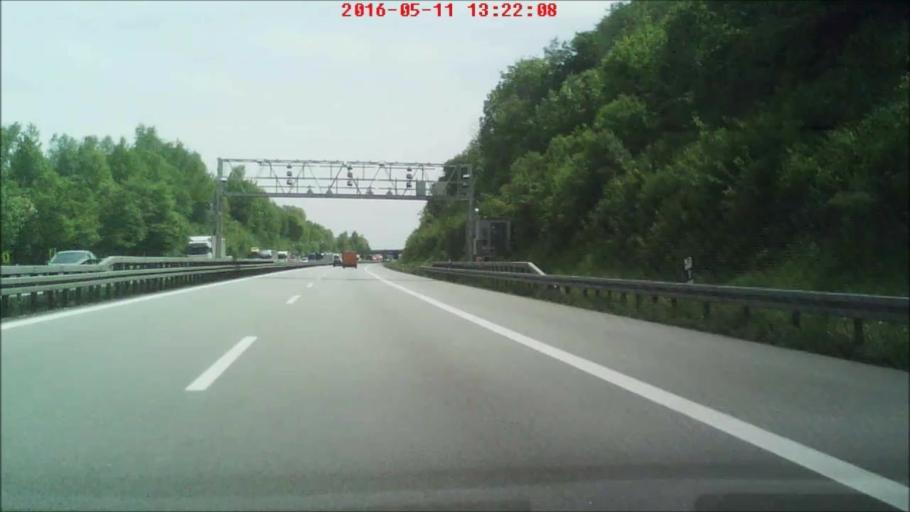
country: AT
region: Upper Austria
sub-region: Politischer Bezirk Scharding
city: Scharding
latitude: 48.4639
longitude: 13.3738
